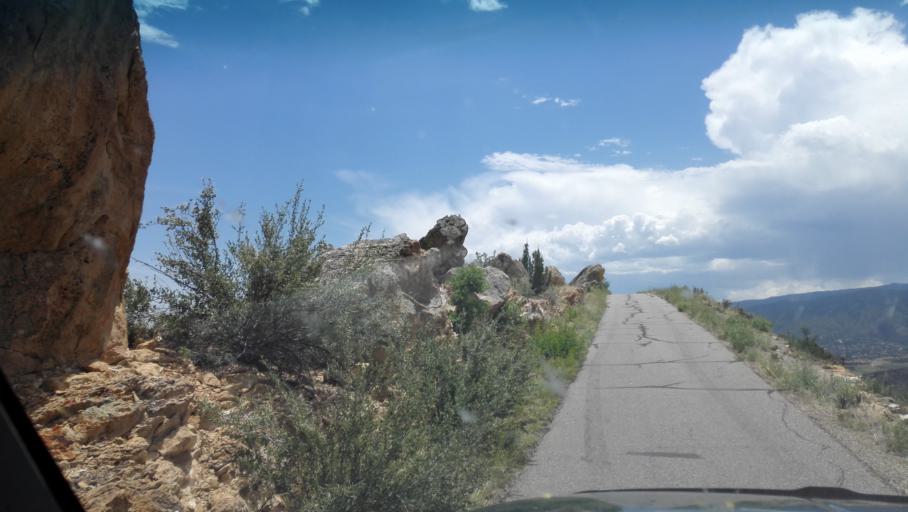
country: US
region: Colorado
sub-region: Fremont County
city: Canon City
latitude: 38.4543
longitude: -105.2496
